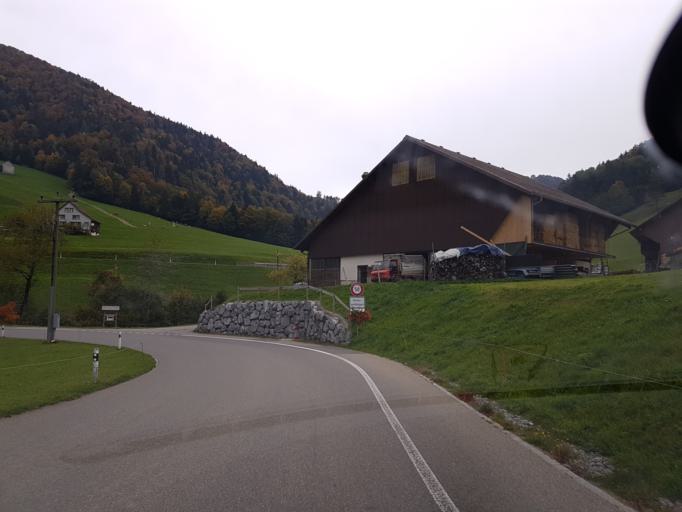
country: CH
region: Saint Gallen
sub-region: Wahlkreis See-Gaster
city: Goldingen
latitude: 47.2890
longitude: 8.9879
